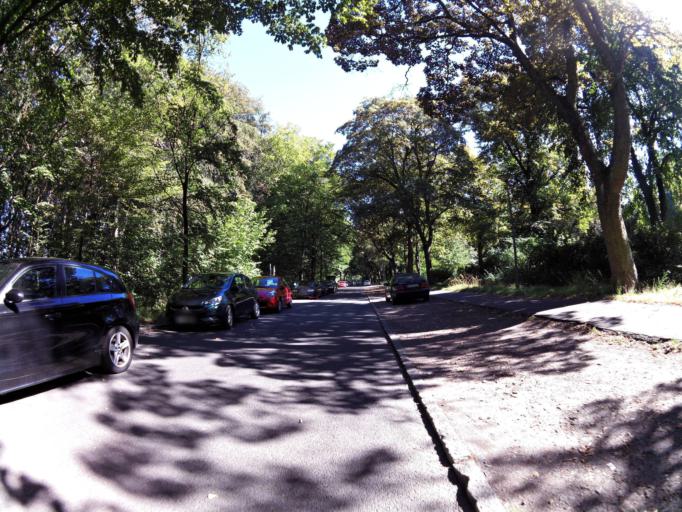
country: DE
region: Berlin
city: Reinickendorf
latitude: 52.5474
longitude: 13.3285
